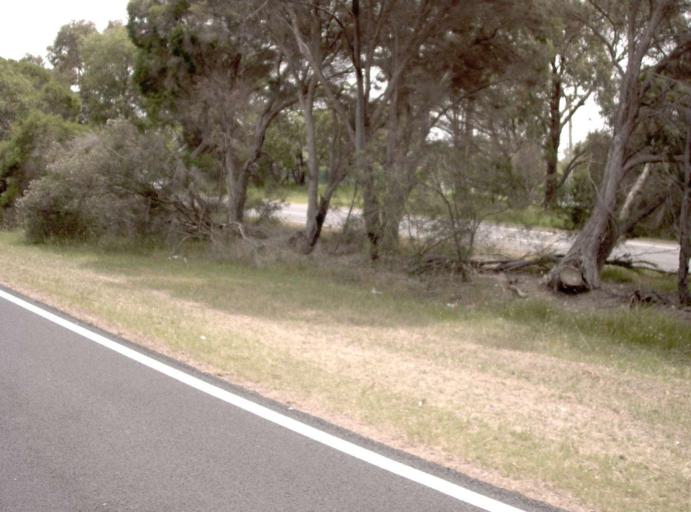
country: AU
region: Victoria
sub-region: Mornington Peninsula
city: Dromana
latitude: -38.3391
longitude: 144.9673
